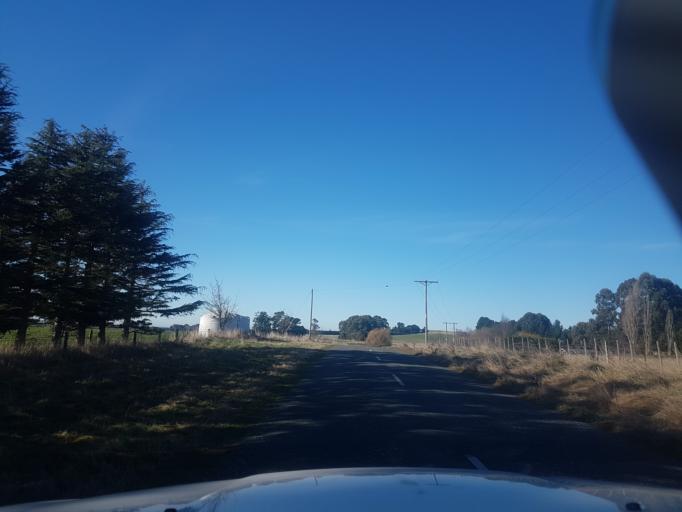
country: NZ
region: Canterbury
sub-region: Timaru District
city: Pleasant Point
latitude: -44.2884
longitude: 171.0775
